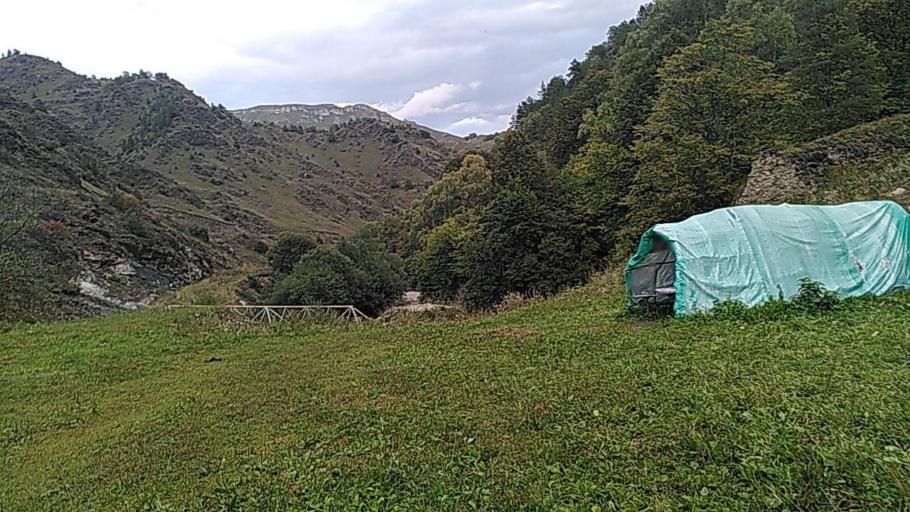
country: RU
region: Kabardino-Balkariya
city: Kamennomostskoye
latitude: 43.7194
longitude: 42.8433
